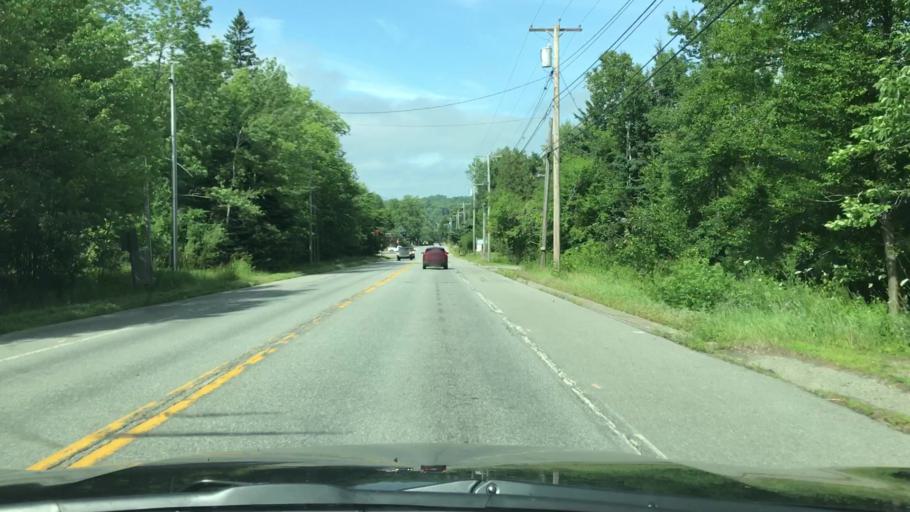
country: US
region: Maine
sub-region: Hancock County
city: Bucksport
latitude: 44.5617
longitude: -68.7921
